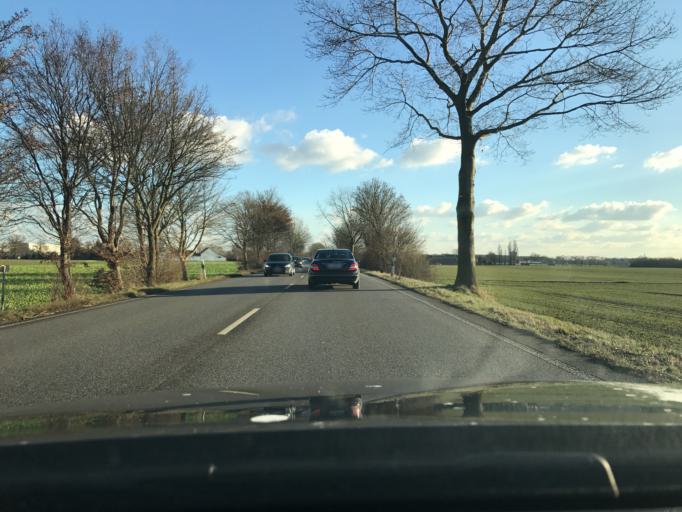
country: DE
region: North Rhine-Westphalia
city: Tonisvorst
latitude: 51.3558
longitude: 6.5101
